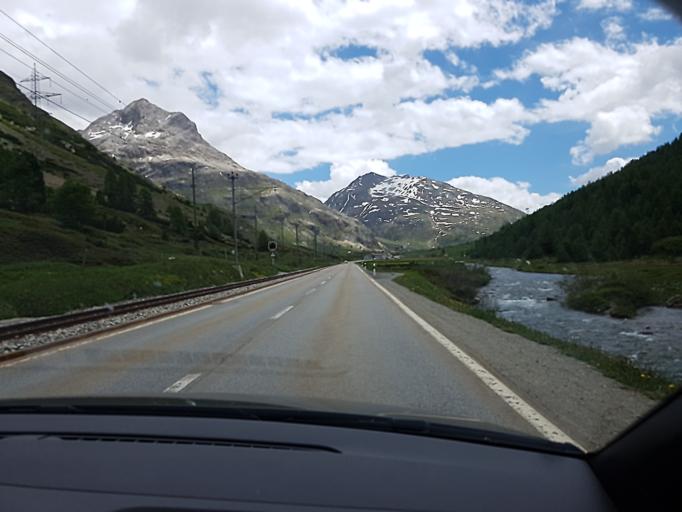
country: CH
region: Grisons
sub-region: Maloja District
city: Pontresina
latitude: 46.4482
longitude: 9.9602
